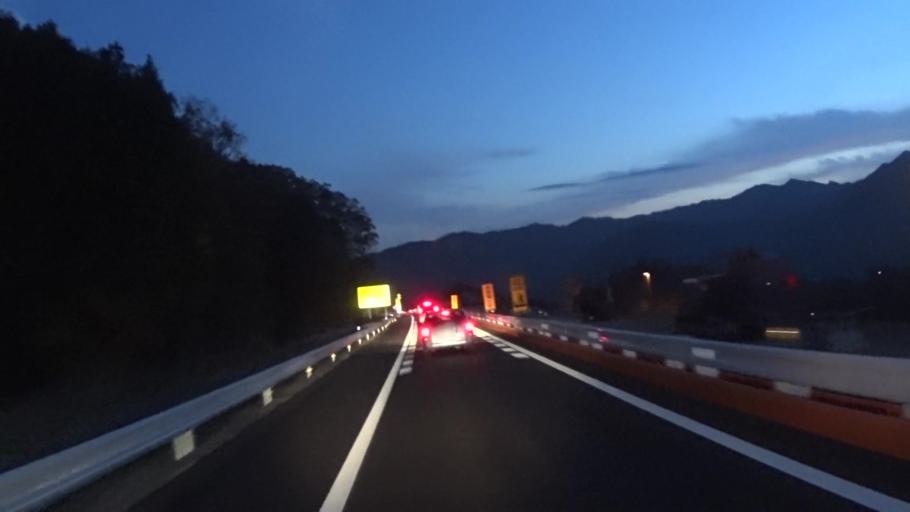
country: JP
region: Kyoto
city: Ayabe
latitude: 35.2827
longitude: 135.3374
